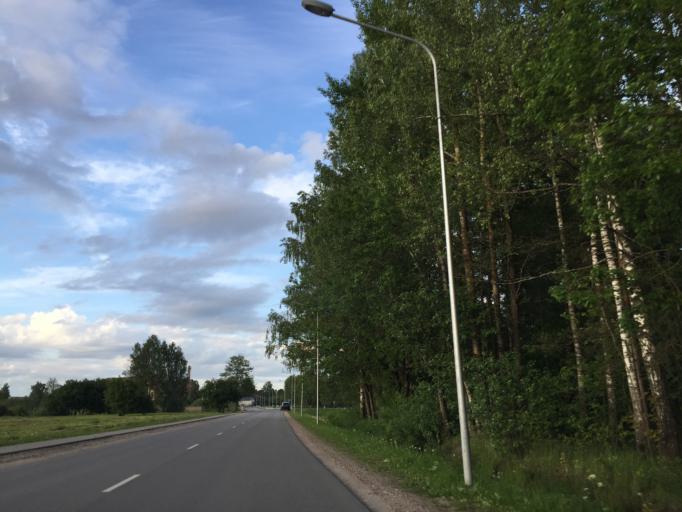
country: LV
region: Babite
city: Pinki
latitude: 56.9407
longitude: 23.8993
